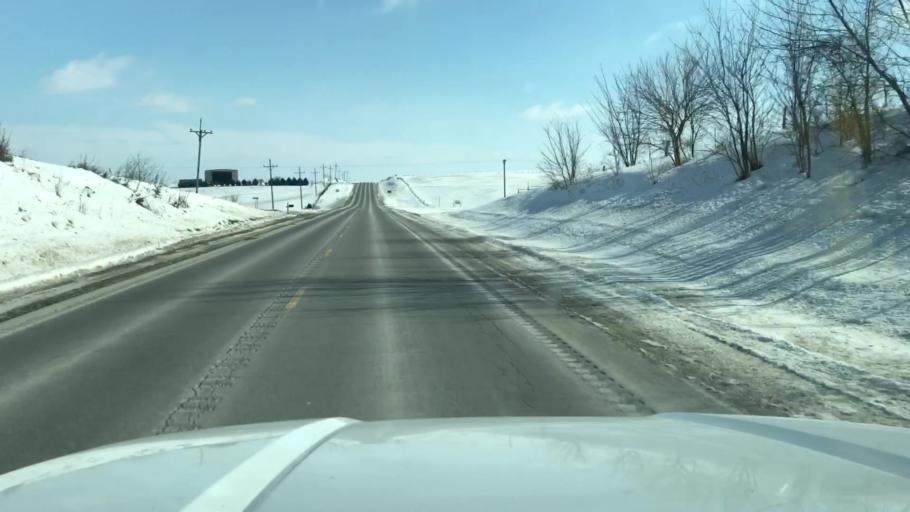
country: US
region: Missouri
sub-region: Nodaway County
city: Maryville
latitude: 40.3440
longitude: -94.7431
